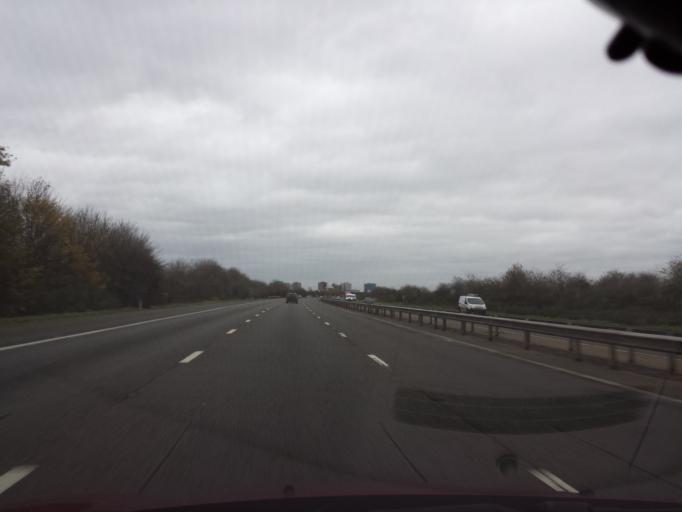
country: GB
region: England
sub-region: Surrey
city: Shepperton
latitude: 51.4077
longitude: -0.4428
